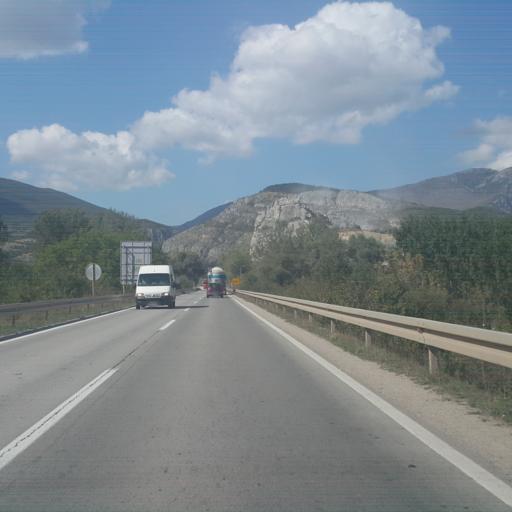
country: RS
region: Central Serbia
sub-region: Nisavski Okrug
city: Svrljig
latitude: 43.3009
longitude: 22.1966
